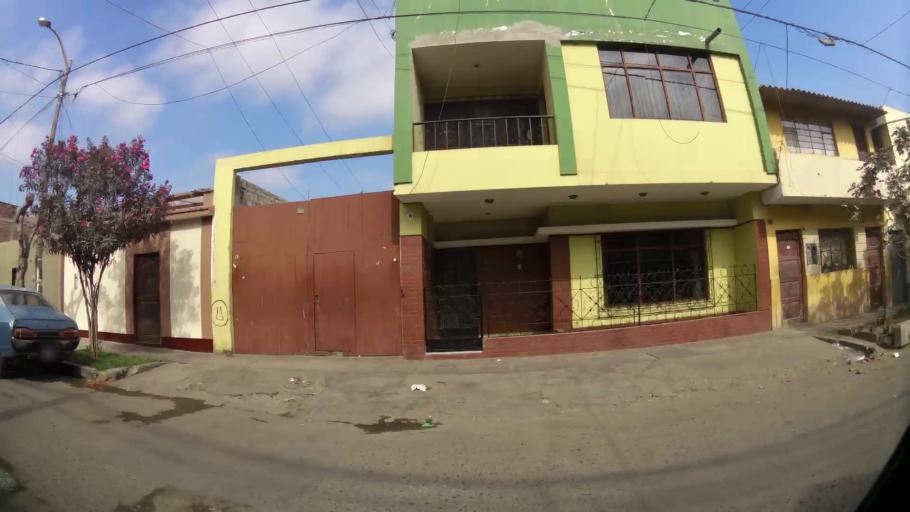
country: PE
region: La Libertad
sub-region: Provincia de Trujillo
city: Trujillo
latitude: -8.1060
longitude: -79.0131
